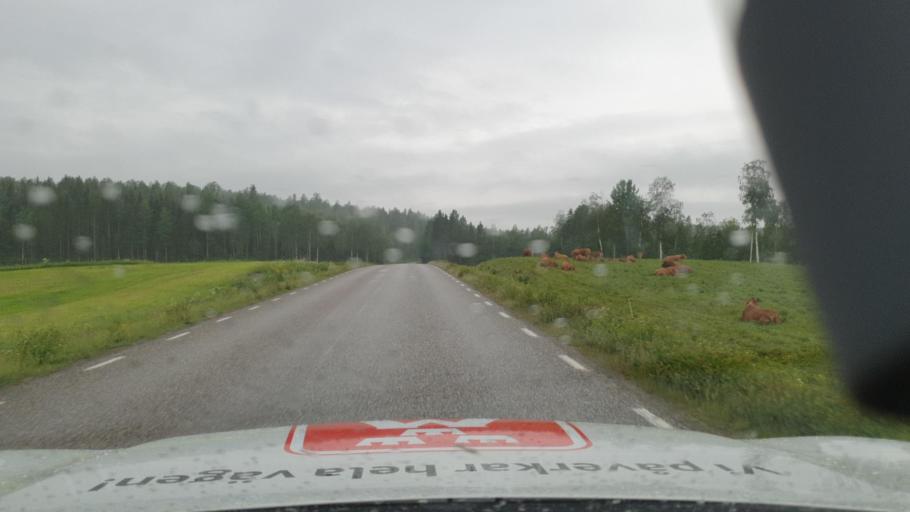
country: SE
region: Vaesterbotten
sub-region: Vannas Kommun
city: Vaennaes
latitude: 63.7896
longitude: 19.5667
